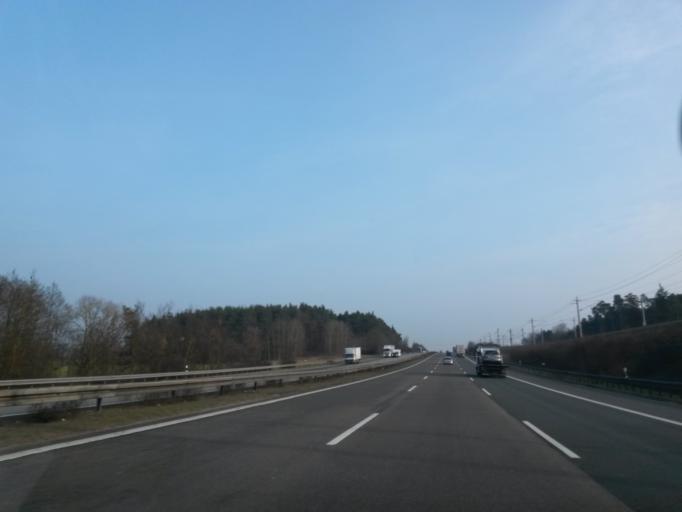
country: DE
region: Bavaria
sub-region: Regierungsbezirk Mittelfranken
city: Allersberg
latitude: 49.2063
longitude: 11.2353
